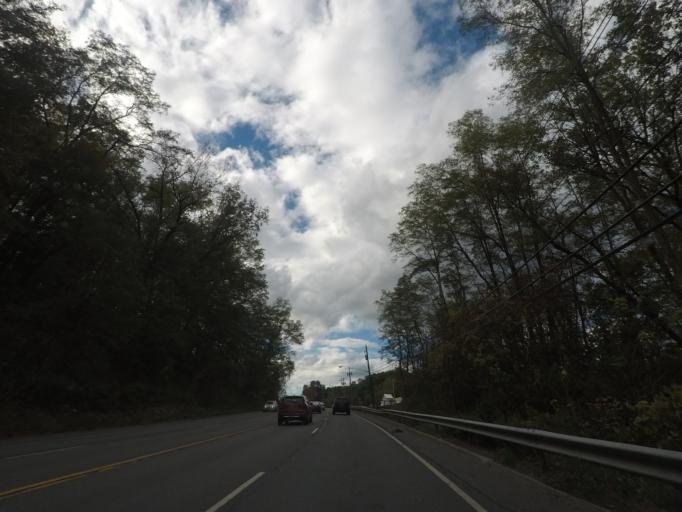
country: US
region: New York
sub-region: Albany County
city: Westmere
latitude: 42.7059
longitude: -73.9154
